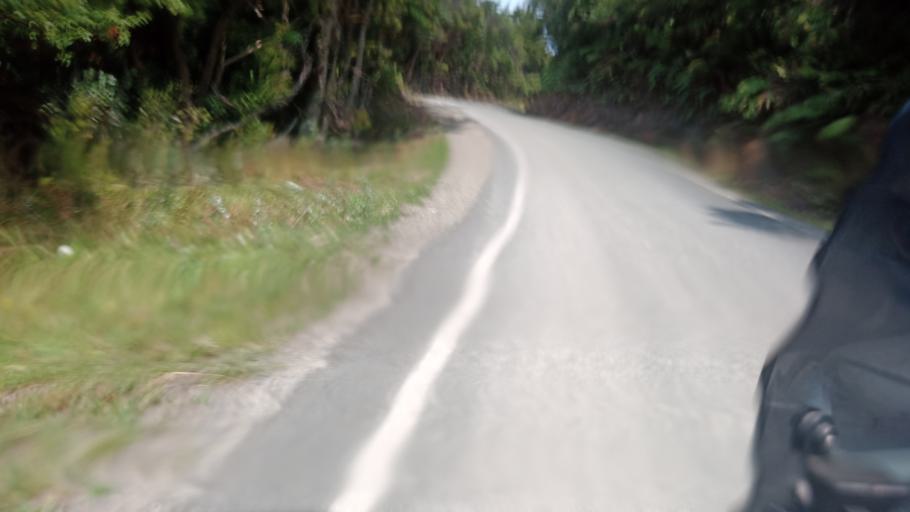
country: NZ
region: Bay of Plenty
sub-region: Opotiki District
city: Opotiki
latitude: -37.6340
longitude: 178.1410
